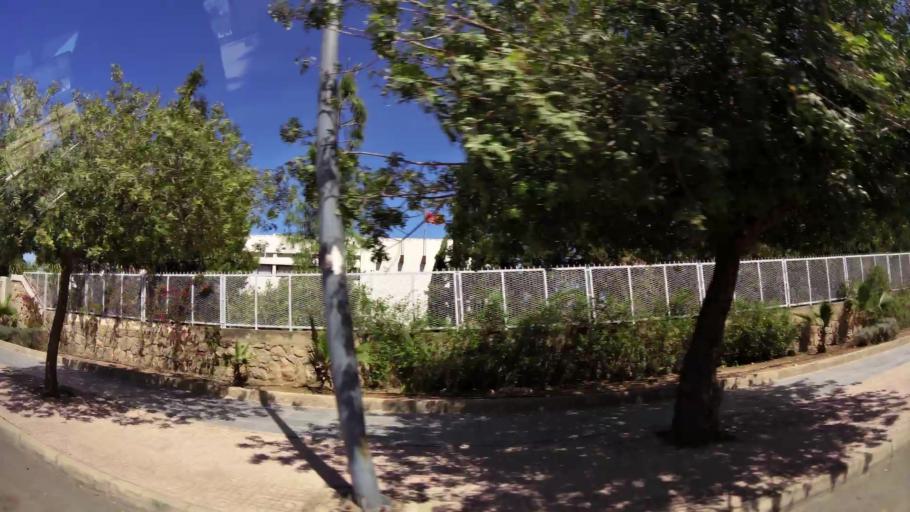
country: MA
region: Oriental
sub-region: Oujda-Angad
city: Oujda
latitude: 34.6543
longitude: -1.9004
